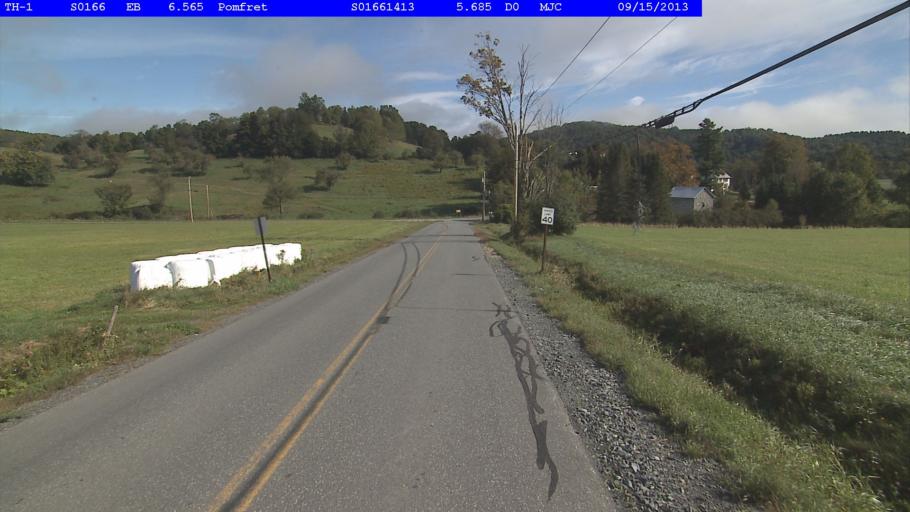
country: US
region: Vermont
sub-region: Windsor County
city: Woodstock
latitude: 43.7218
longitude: -72.5019
